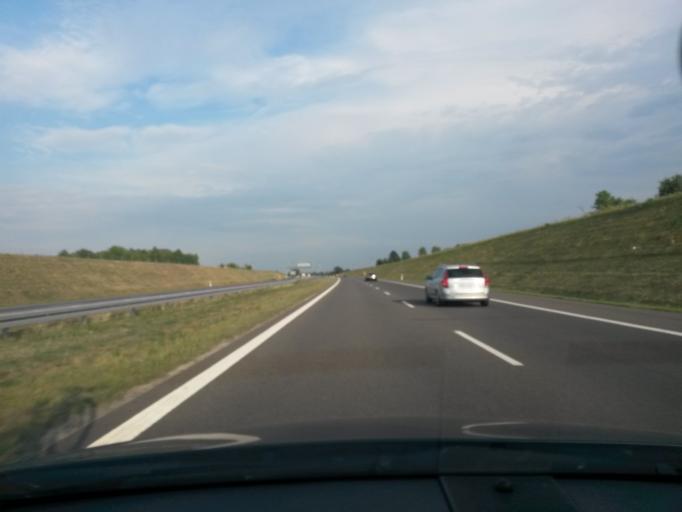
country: PL
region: Lodz Voivodeship
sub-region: Powiat zgierski
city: Zgierz
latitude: 51.9032
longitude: 19.4560
